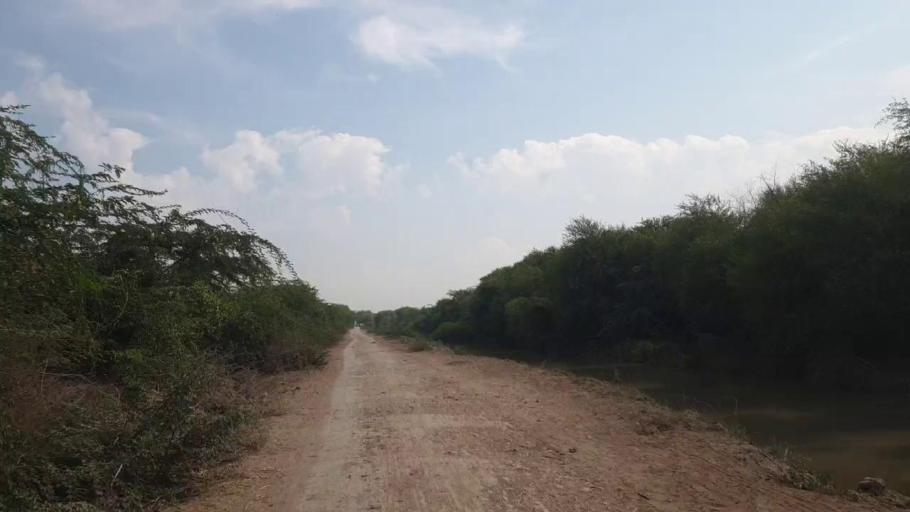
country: PK
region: Sindh
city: Tando Bago
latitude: 24.9266
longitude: 69.0146
